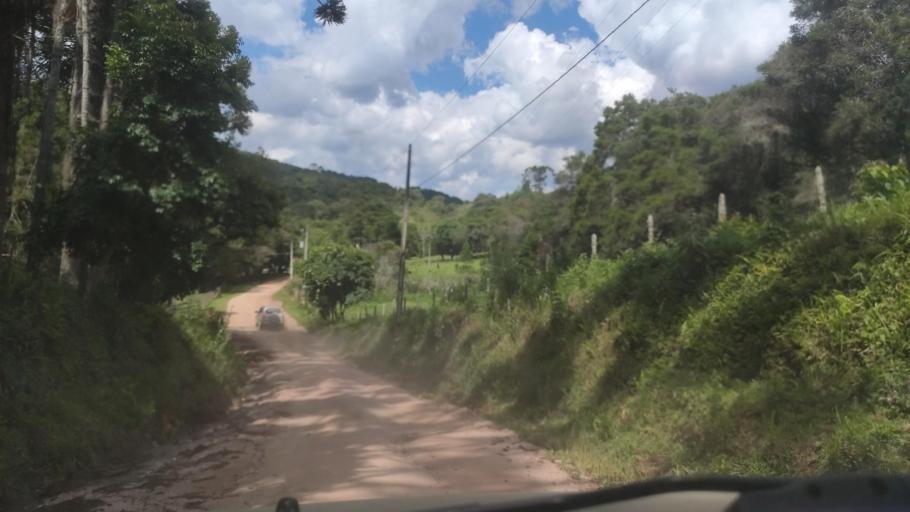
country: BR
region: Minas Gerais
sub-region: Camanducaia
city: Camanducaia
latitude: -22.7671
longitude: -45.9804
